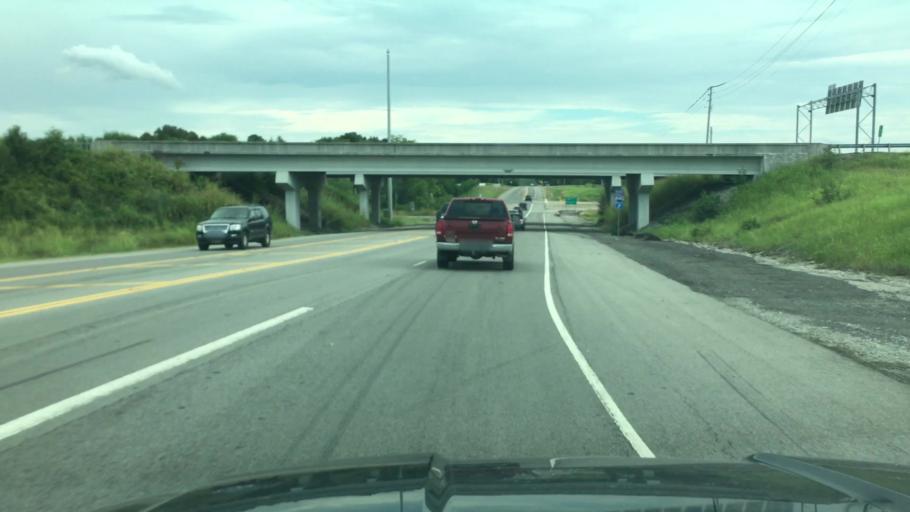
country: US
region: Tennessee
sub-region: Williamson County
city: Thompson's Station
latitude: 35.8225
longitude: -86.8509
